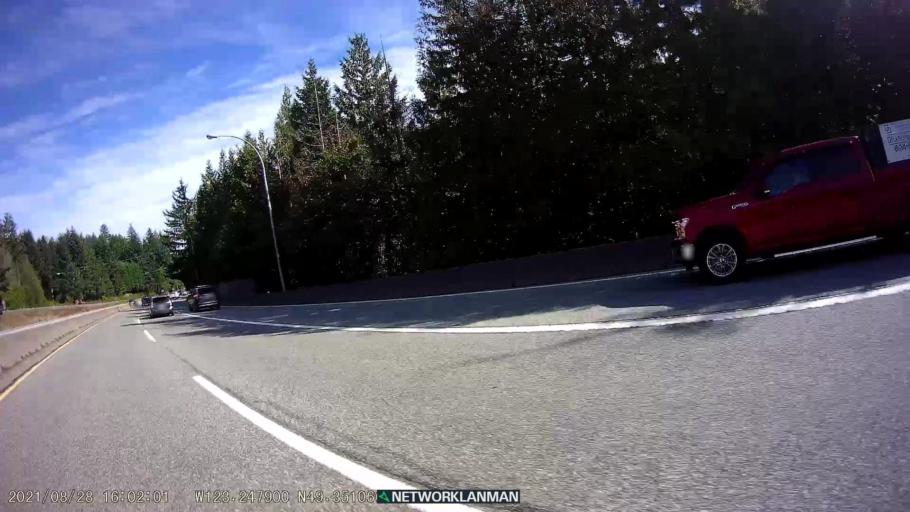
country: CA
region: British Columbia
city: West Vancouver
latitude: 49.3519
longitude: -123.2485
